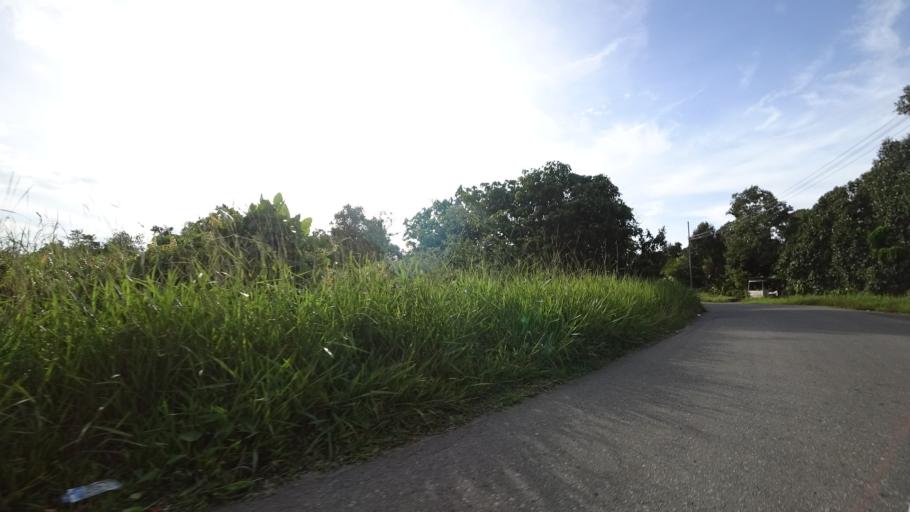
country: BN
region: Brunei and Muara
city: Bandar Seri Begawan
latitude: 4.8162
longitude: 114.8255
